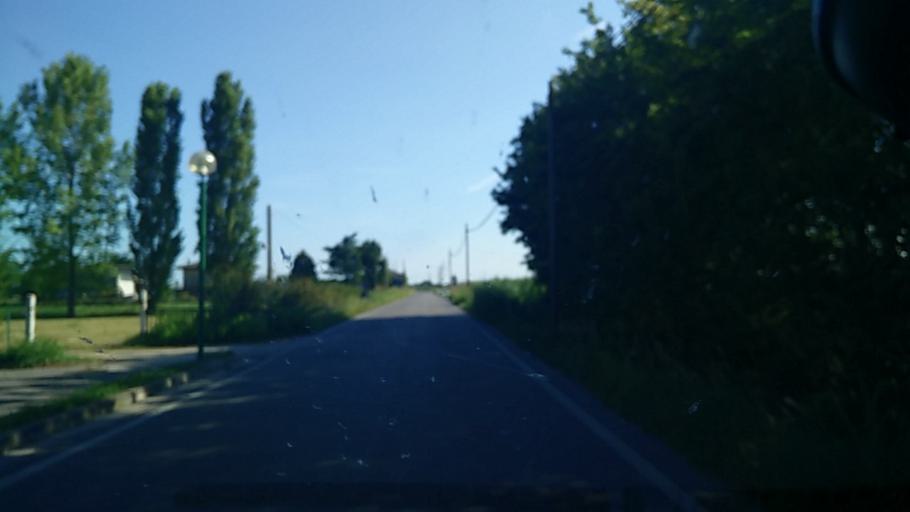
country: IT
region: Veneto
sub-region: Provincia di Treviso
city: Monastier di Treviso
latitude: 45.6772
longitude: 12.4033
